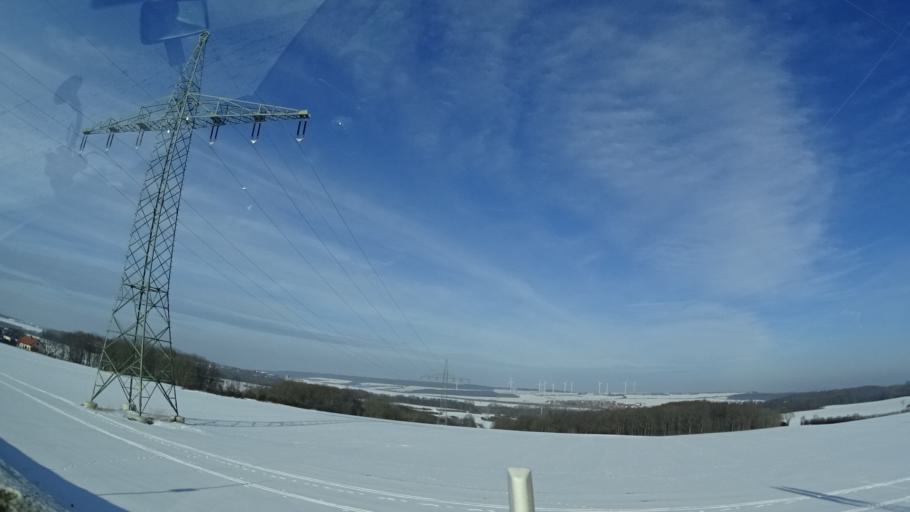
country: DE
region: Thuringia
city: Bucha
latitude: 50.8549
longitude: 11.5080
